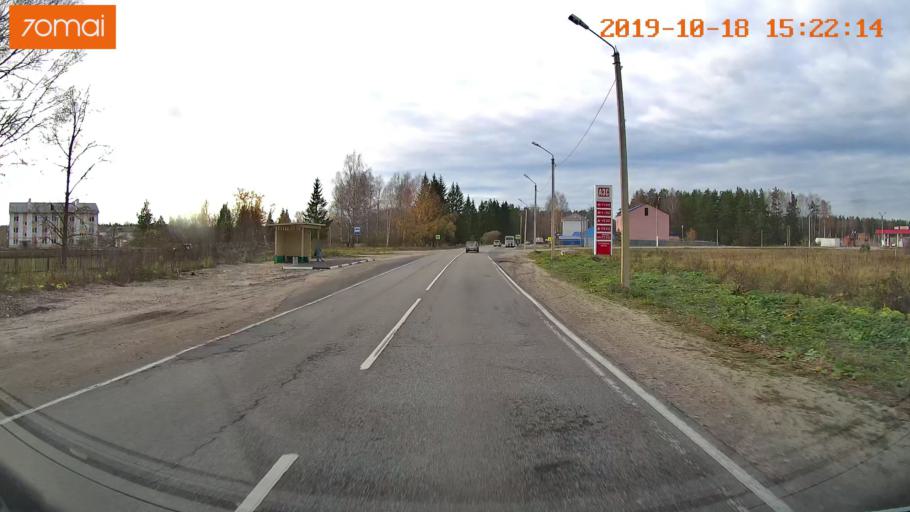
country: RU
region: Vladimir
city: Anopino
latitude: 55.7066
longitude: 40.7347
